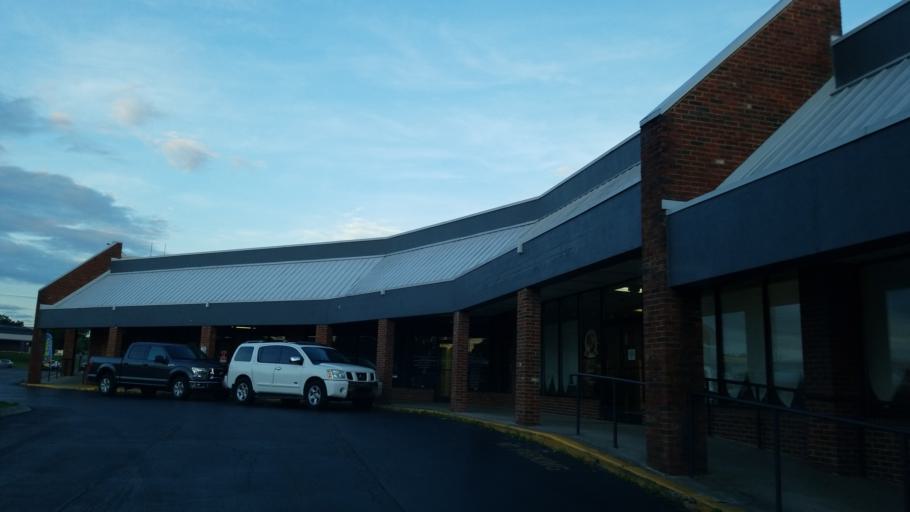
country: US
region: Tennessee
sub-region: Rutherford County
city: La Vergne
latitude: 36.0469
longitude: -86.6500
